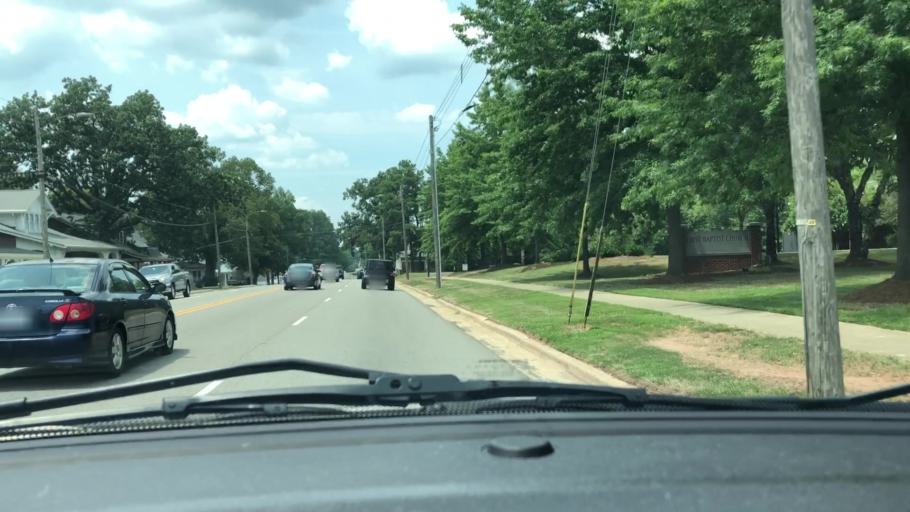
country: US
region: North Carolina
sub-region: Lee County
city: Sanford
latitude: 35.4817
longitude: -79.1820
